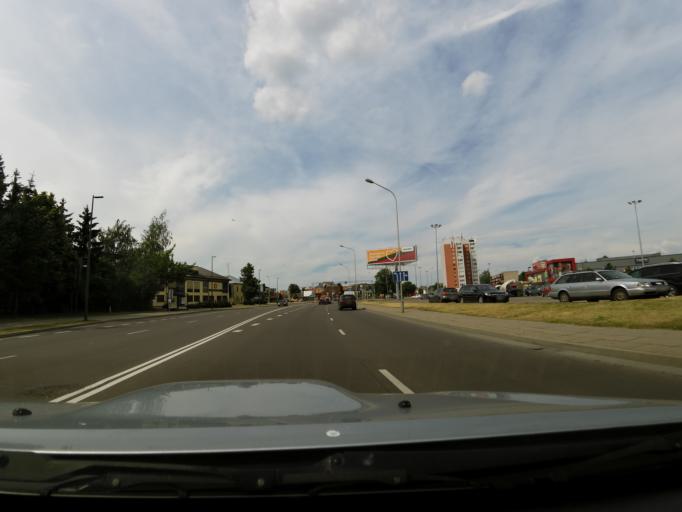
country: LT
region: Marijampoles apskritis
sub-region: Marijampole Municipality
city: Marijampole
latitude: 54.5597
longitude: 23.3537
